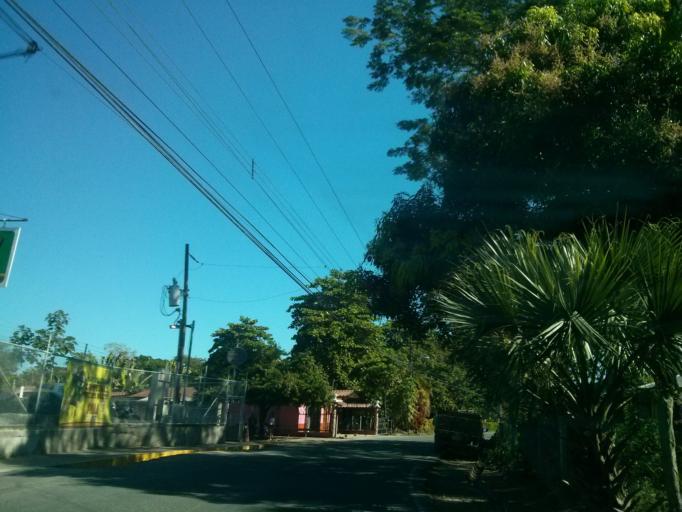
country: CR
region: Puntarenas
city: Paquera
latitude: 9.8212
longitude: -84.9327
